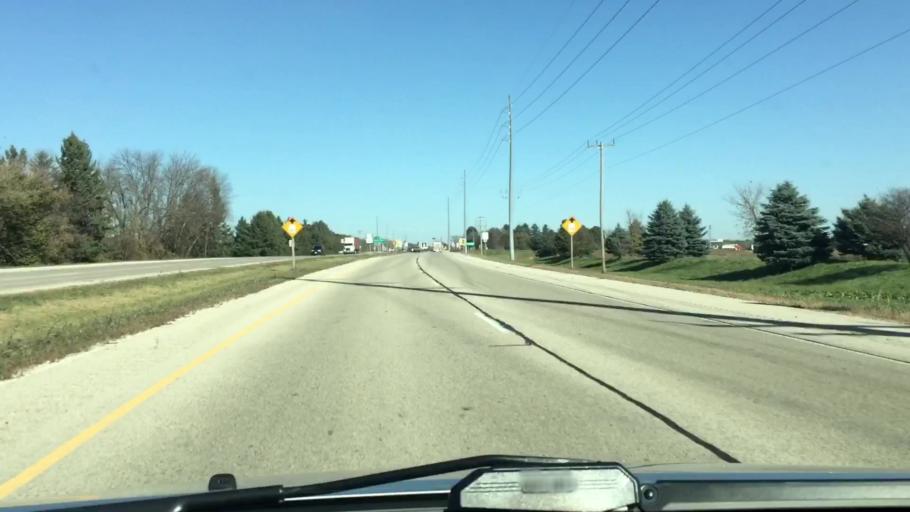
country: US
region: Wisconsin
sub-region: Waukesha County
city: Sussex
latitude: 43.1083
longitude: -88.2102
